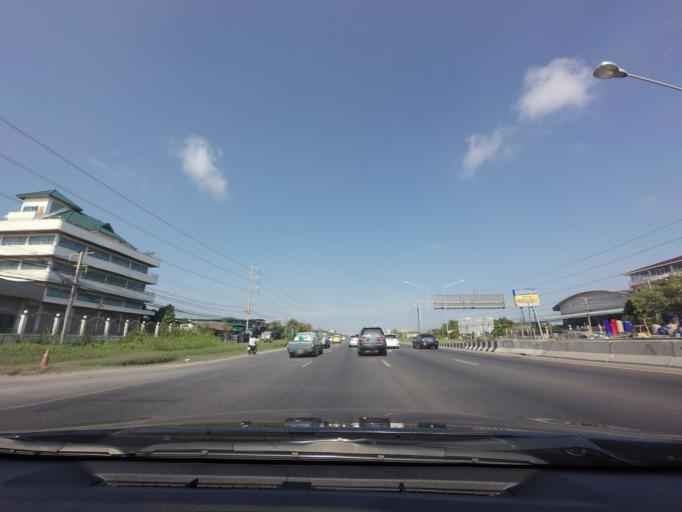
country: TH
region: Samut Sakhon
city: Samut Sakhon
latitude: 13.5271
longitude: 100.1917
